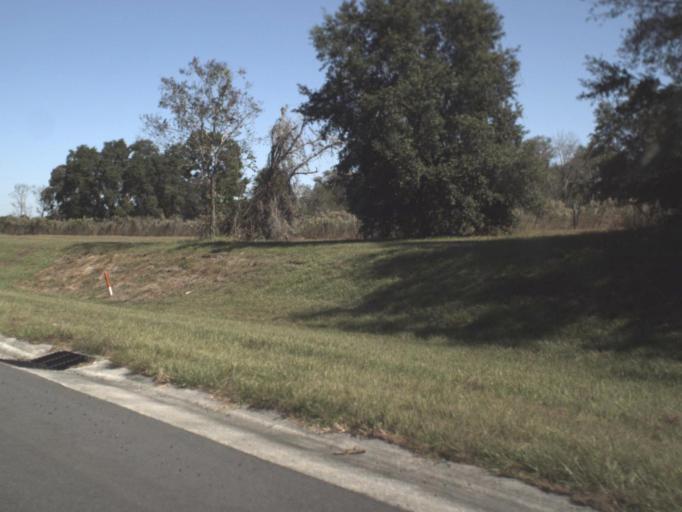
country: US
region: Florida
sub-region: Hernando County
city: Brookridge
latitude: 28.6203
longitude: -82.4931
